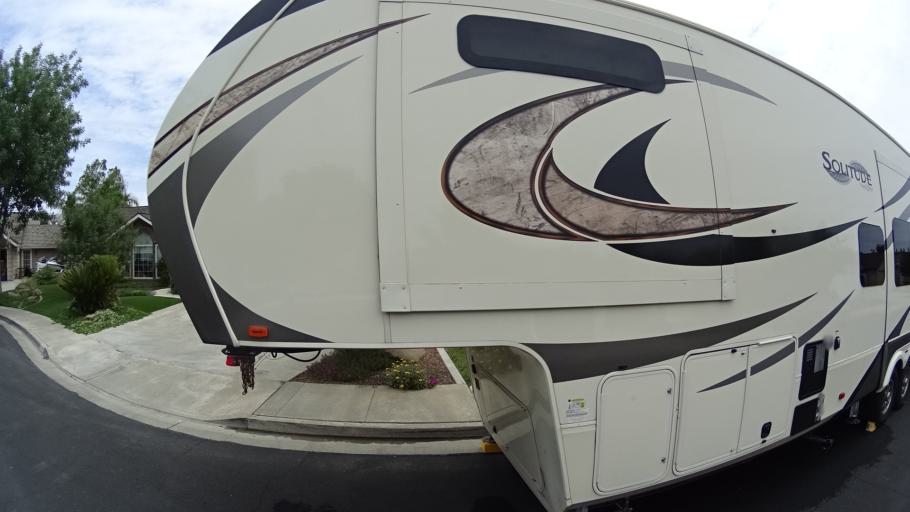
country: US
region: California
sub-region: Kings County
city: Lucerne
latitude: 36.3603
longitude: -119.6387
